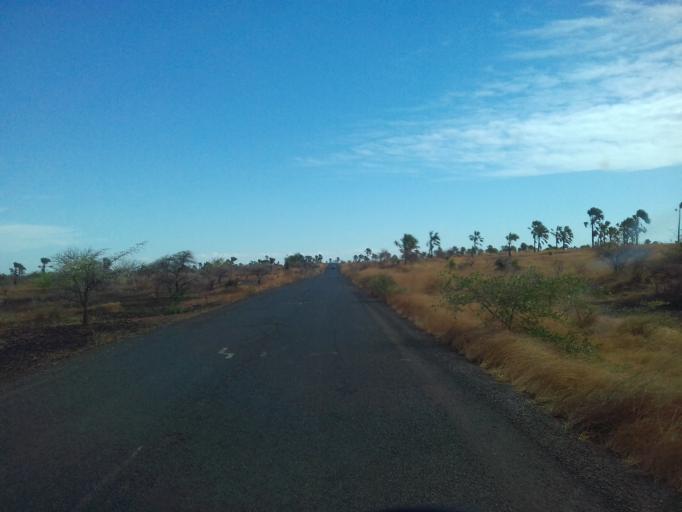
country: MG
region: Sofia
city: Antsohihy
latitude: -15.2521
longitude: 47.8057
